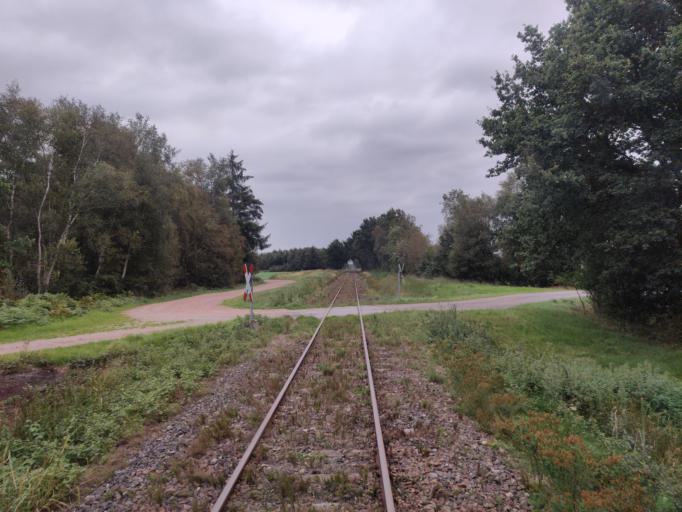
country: DE
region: Lower Saxony
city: Oerel
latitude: 53.4814
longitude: 9.0859
